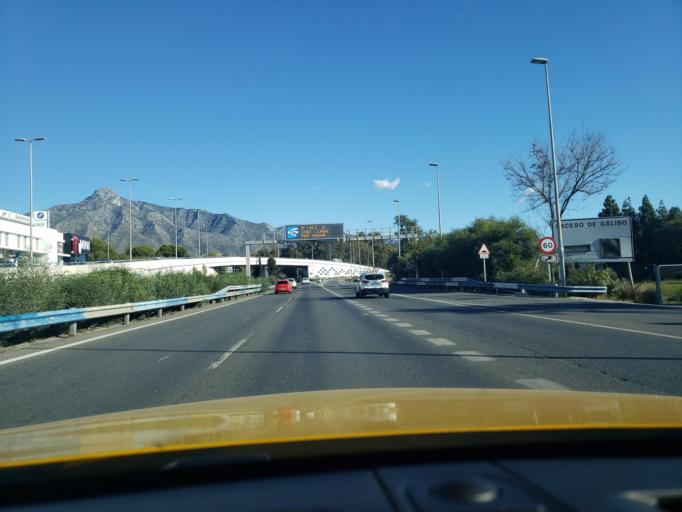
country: ES
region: Andalusia
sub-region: Provincia de Malaga
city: Marbella
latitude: 36.4952
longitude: -4.9498
